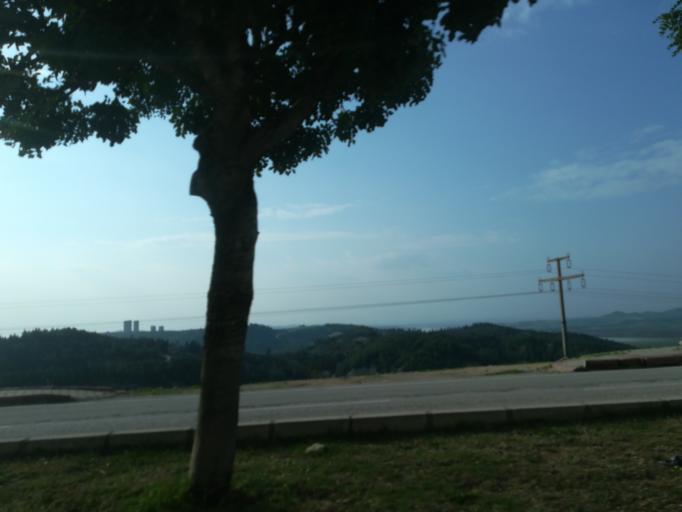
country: TR
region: Adana
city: Adana
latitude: 37.0697
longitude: 35.3790
